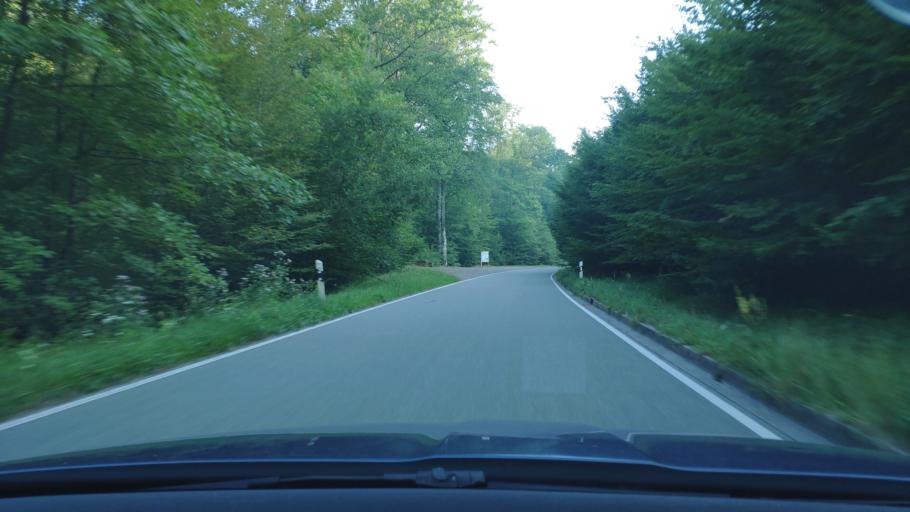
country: DE
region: Rheinland-Pfalz
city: Fischbach
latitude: 49.0634
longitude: 7.7175
